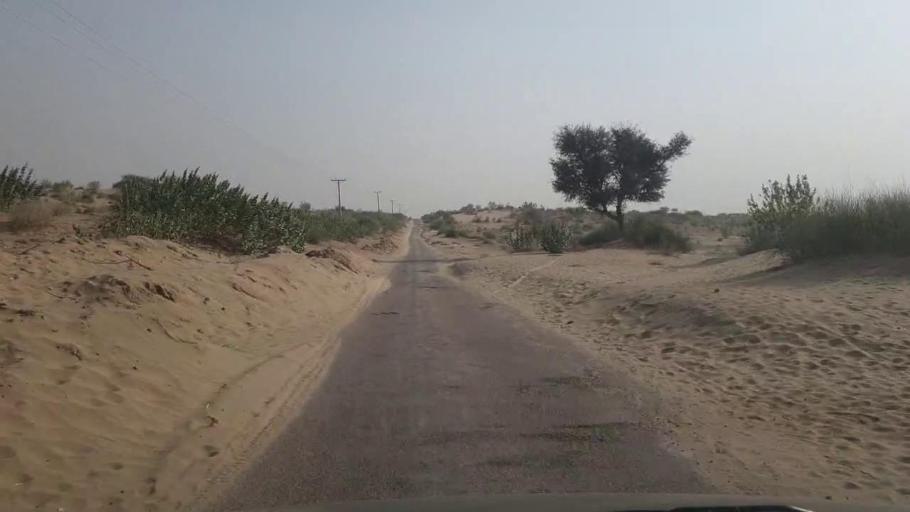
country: PK
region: Sindh
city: Chor
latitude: 25.5539
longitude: 69.9583
